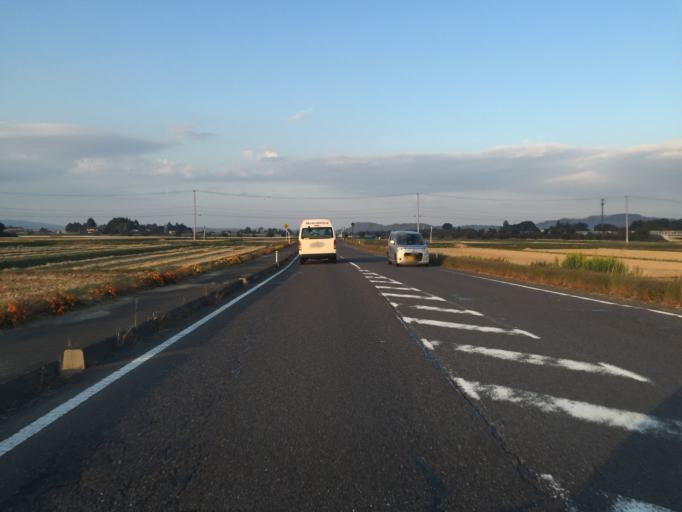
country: JP
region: Fukushima
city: Motomiya
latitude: 37.5303
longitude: 140.3784
